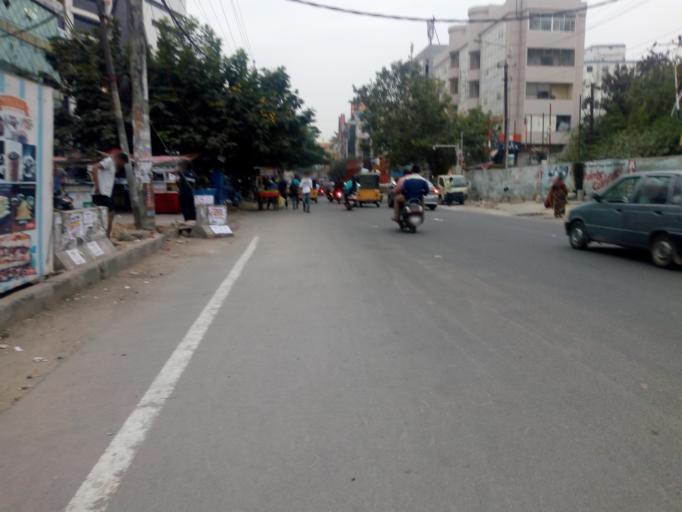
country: IN
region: Telangana
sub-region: Hyderabad
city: Hyderabad
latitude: 17.4373
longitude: 78.4472
